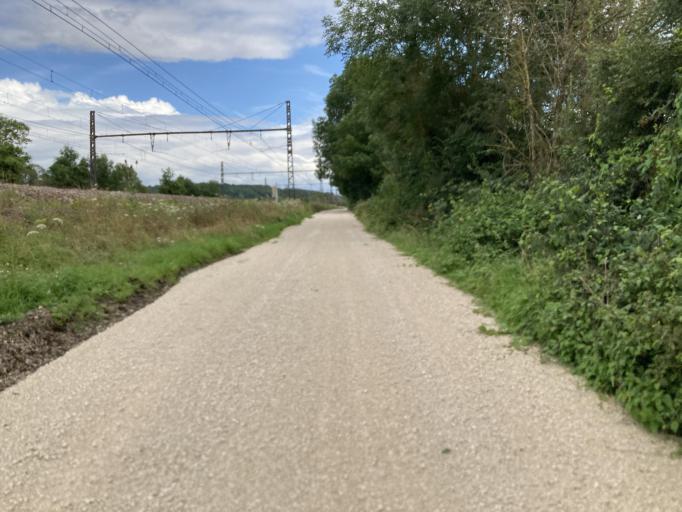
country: FR
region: Bourgogne
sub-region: Departement de la Cote-d'Or
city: Montbard
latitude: 47.6164
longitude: 4.3765
